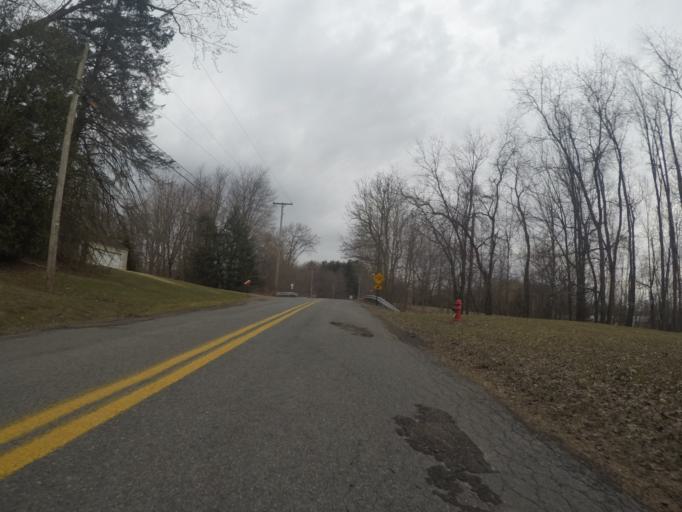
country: US
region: Ohio
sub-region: Portage County
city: Ravenna
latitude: 41.1686
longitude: -81.2848
